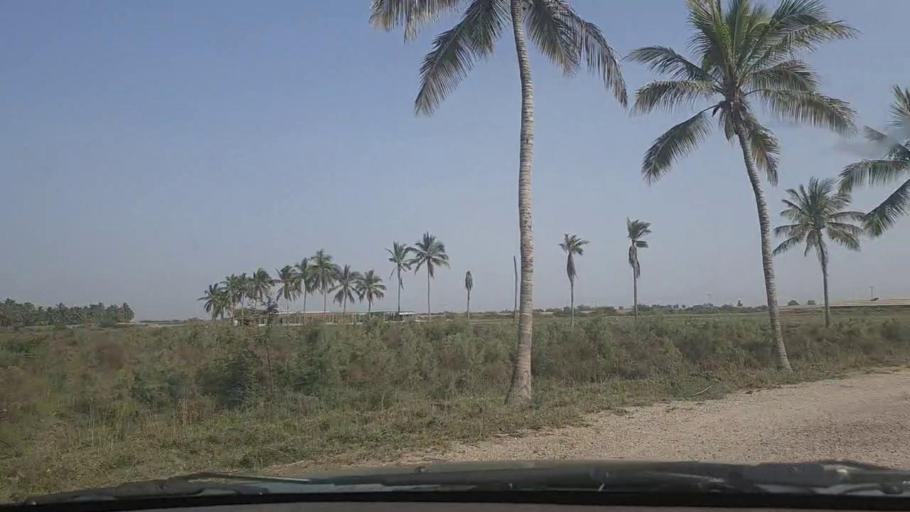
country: PK
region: Sindh
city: Keti Bandar
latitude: 24.1996
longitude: 67.5492
